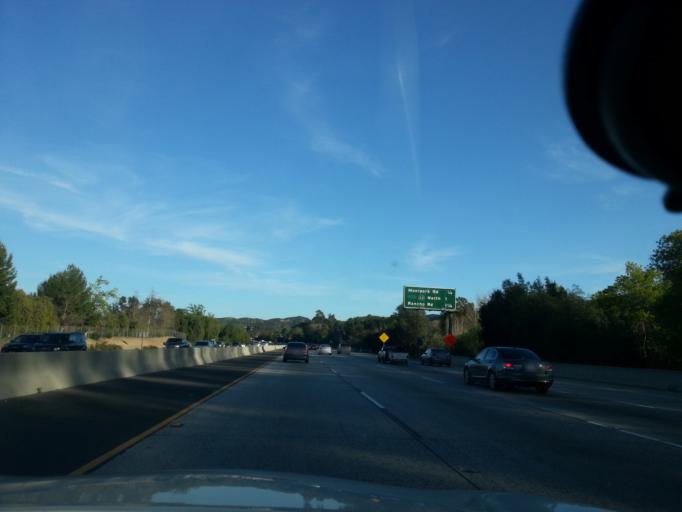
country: US
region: California
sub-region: Ventura County
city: Thousand Oaks
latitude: 34.1800
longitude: -118.8845
